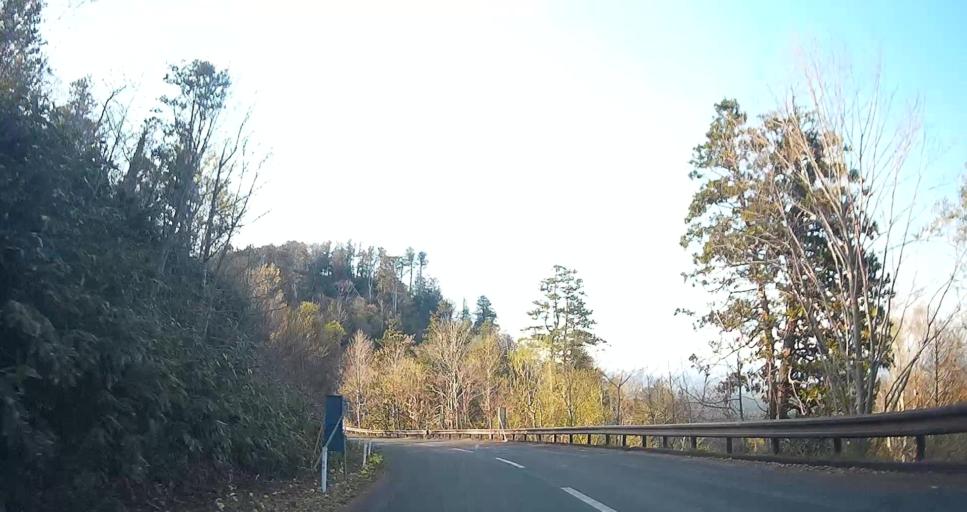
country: JP
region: Aomori
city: Mutsu
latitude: 41.3090
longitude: 141.1134
